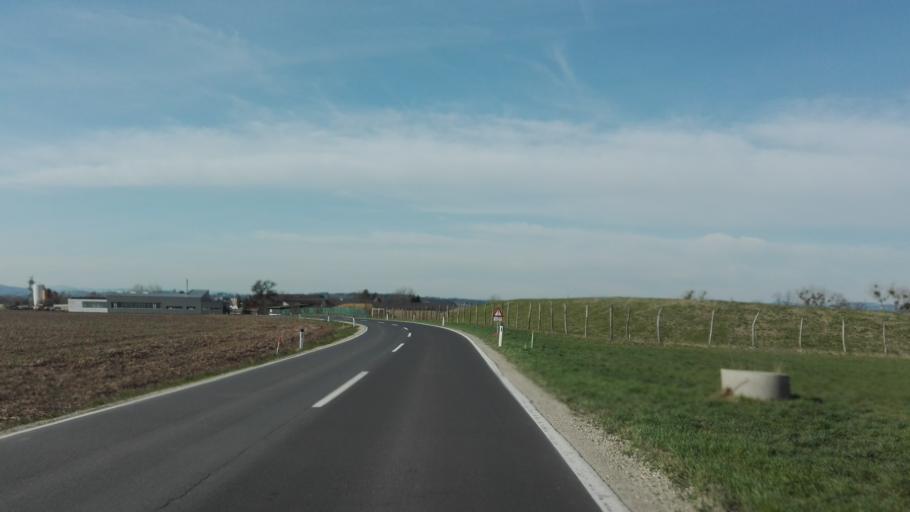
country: AT
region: Lower Austria
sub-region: Politischer Bezirk Amstetten
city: Ennsdorf
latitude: 48.2117
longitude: 14.5439
